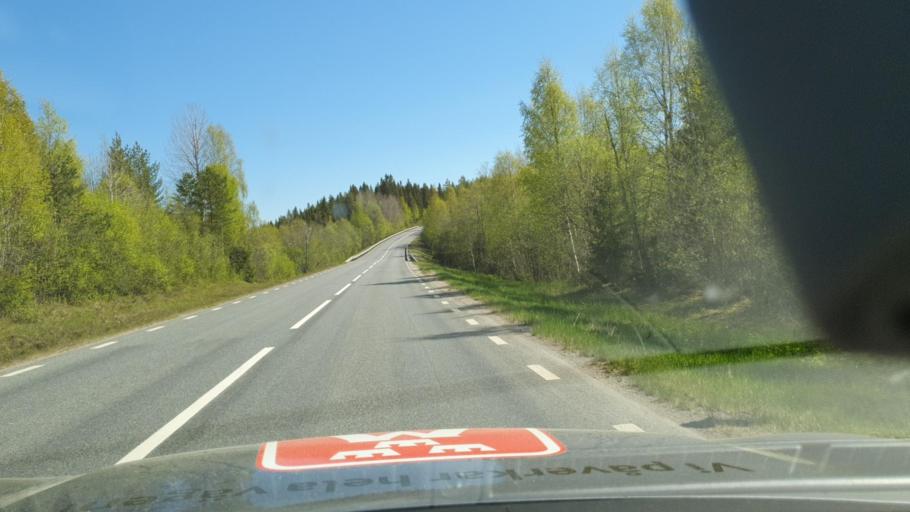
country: SE
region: Vaesternorrland
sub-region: OErnskoeldsviks Kommun
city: Ornskoldsvik
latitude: 63.6949
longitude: 18.5155
